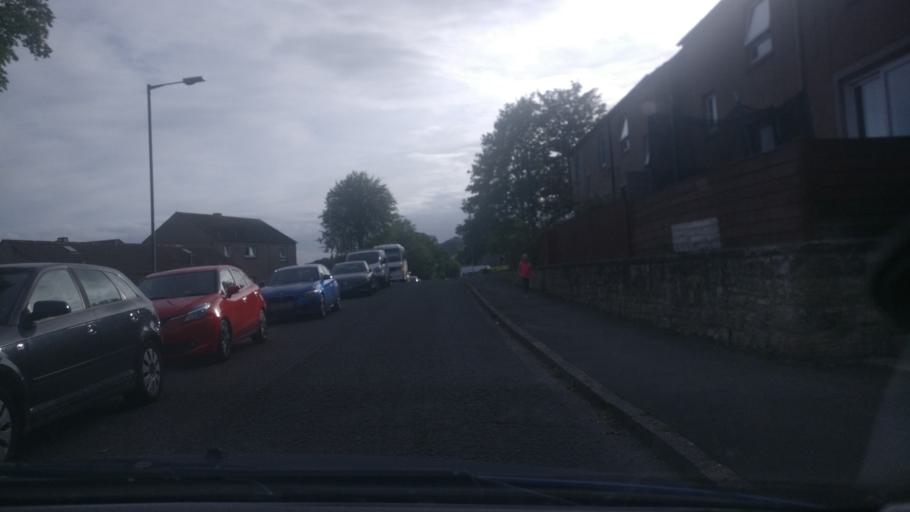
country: GB
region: Scotland
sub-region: The Scottish Borders
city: Hawick
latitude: 55.4335
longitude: -2.7836
